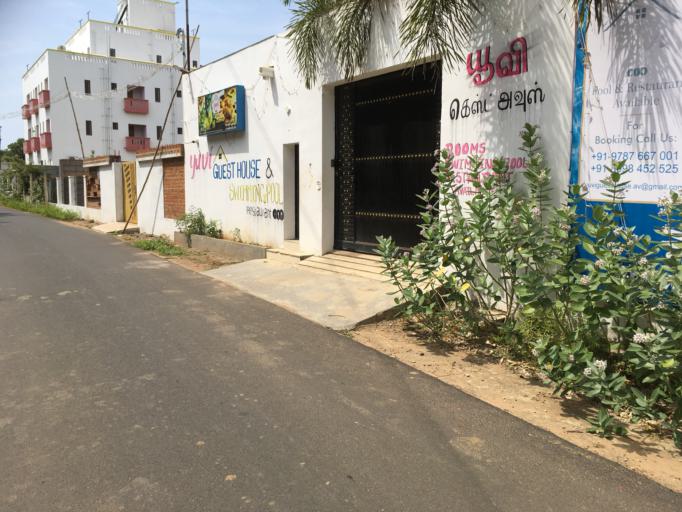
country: IN
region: Tamil Nadu
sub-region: Villupuram
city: Auroville
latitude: 12.0052
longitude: 79.7973
